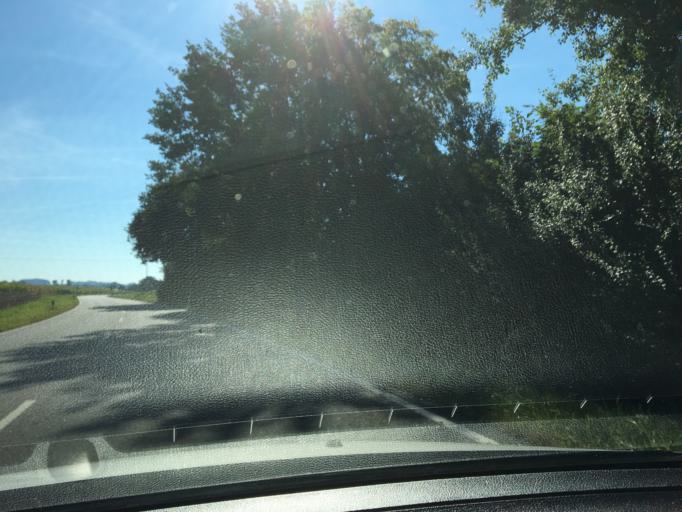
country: DE
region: Bavaria
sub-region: Upper Bavaria
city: Aham
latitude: 48.3509
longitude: 12.1910
